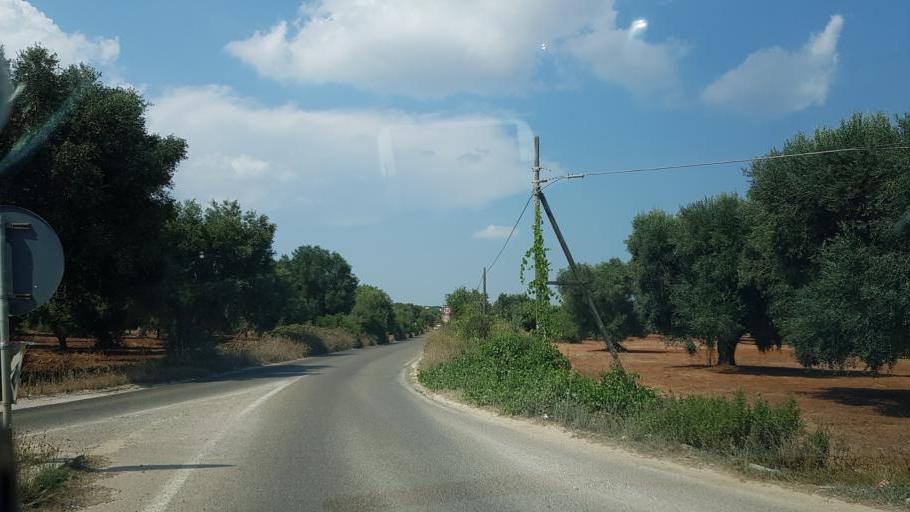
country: IT
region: Apulia
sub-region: Provincia di Taranto
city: Maruggio
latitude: 40.3215
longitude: 17.6312
